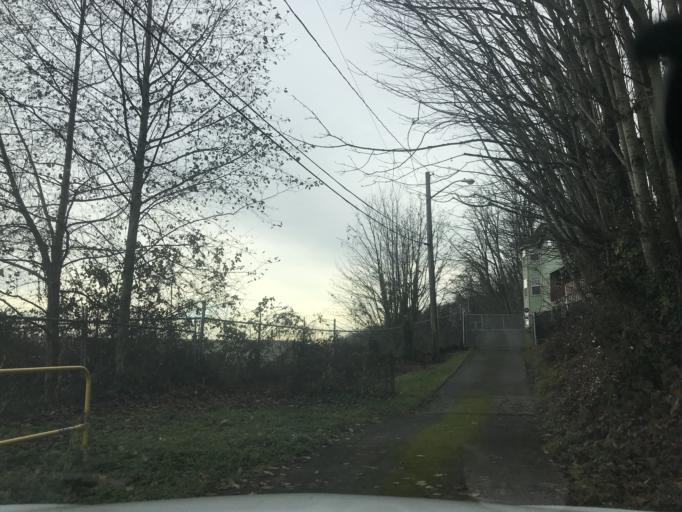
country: US
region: Washington
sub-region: King County
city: Seattle
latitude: 47.5667
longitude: -122.3548
